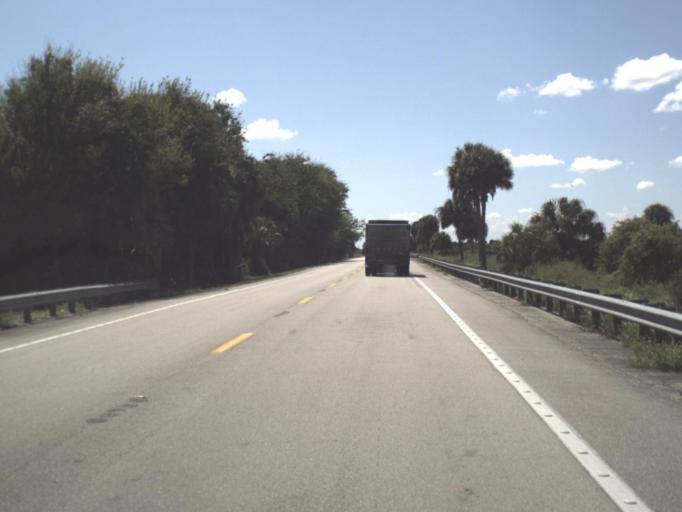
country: US
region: Florida
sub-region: Glades County
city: Buckhead Ridge
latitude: 27.1003
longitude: -80.9513
